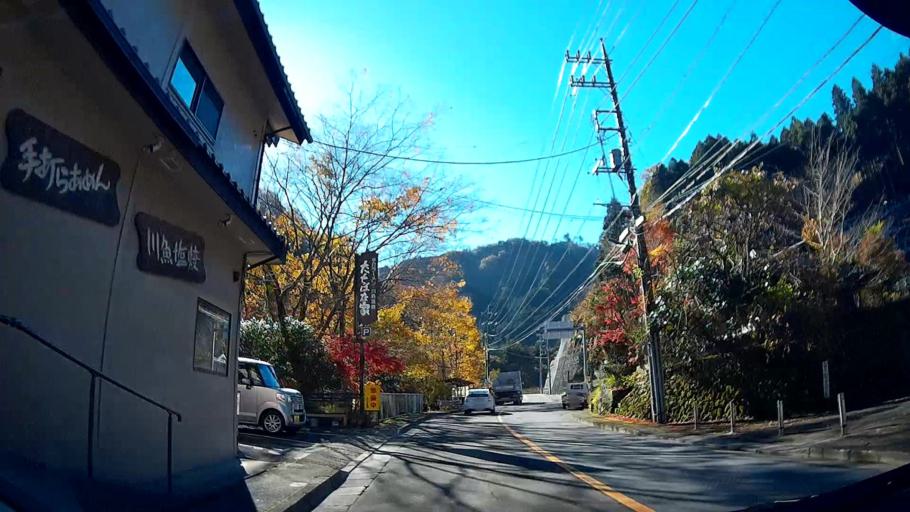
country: JP
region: Tokyo
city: Itsukaichi
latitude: 35.7258
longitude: 139.1474
